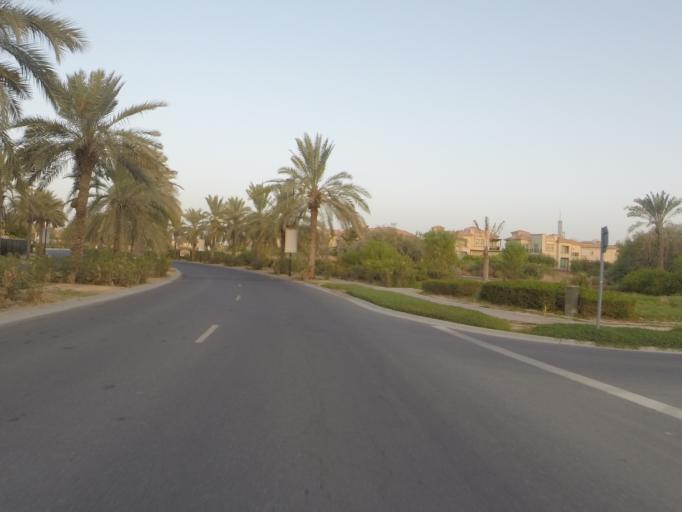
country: AE
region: Dubai
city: Dubai
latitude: 25.0550
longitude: 55.1626
